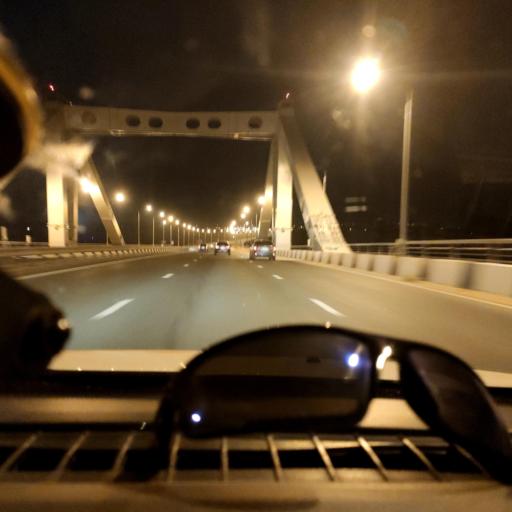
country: RU
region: Samara
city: Rozhdestveno
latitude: 53.1746
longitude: 50.0856
